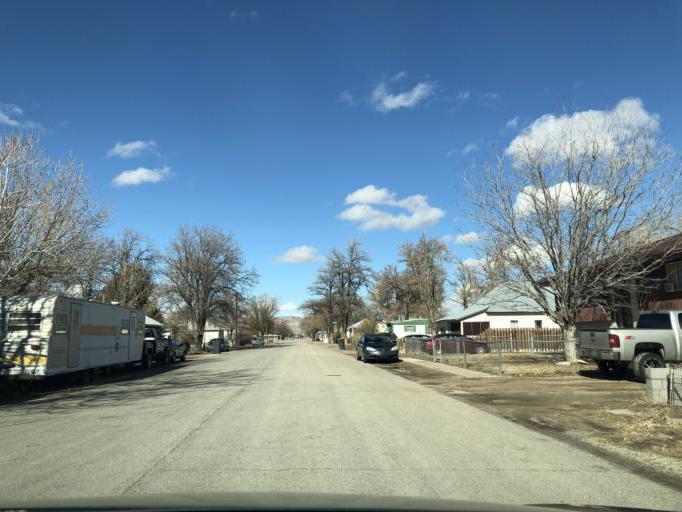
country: US
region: Utah
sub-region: Carbon County
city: East Carbon City
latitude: 38.9928
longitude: -110.1610
